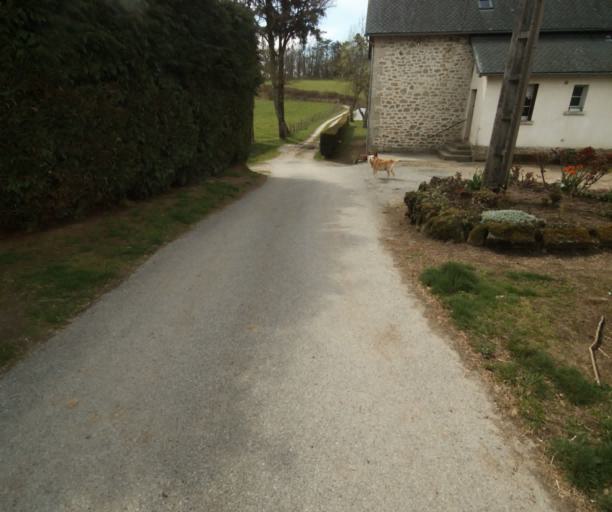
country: FR
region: Limousin
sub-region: Departement de la Correze
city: Correze
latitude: 45.3861
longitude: 1.8975
